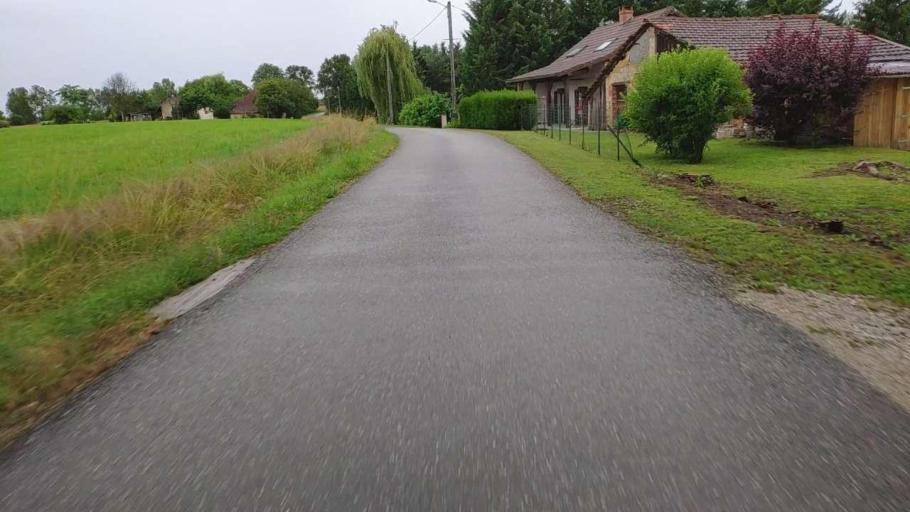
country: FR
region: Franche-Comte
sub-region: Departement du Jura
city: Chaussin
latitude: 46.8811
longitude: 5.4151
